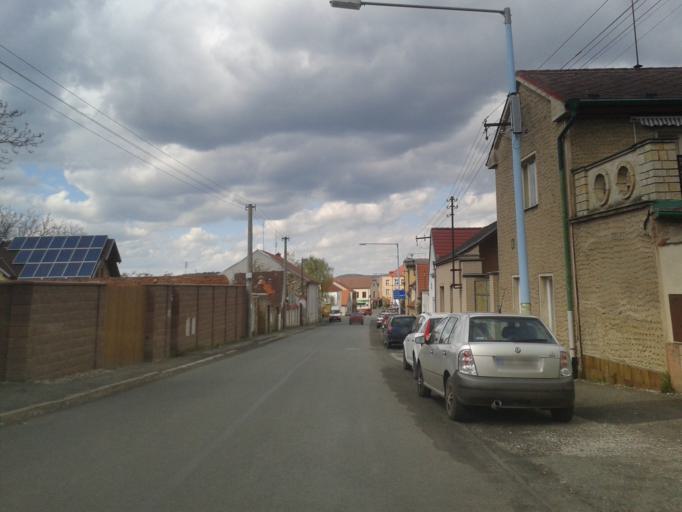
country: CZ
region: Central Bohemia
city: Revnice
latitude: 49.9025
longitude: 14.1468
